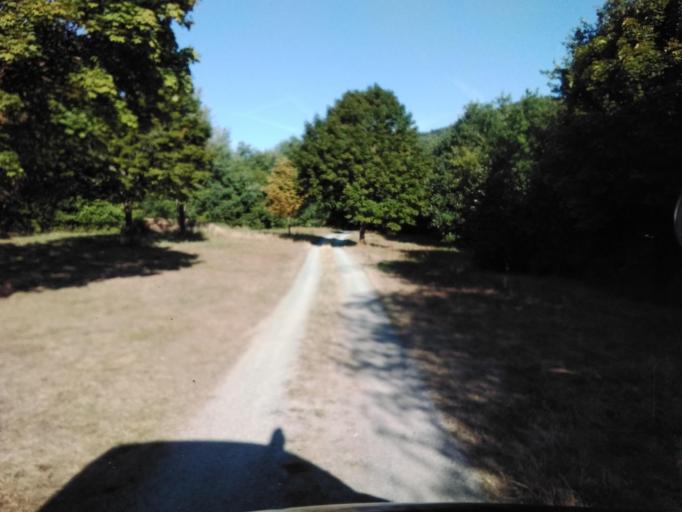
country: DE
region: Bavaria
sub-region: Regierungsbezirk Unterfranken
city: Faulbach
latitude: 49.7863
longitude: 9.4287
